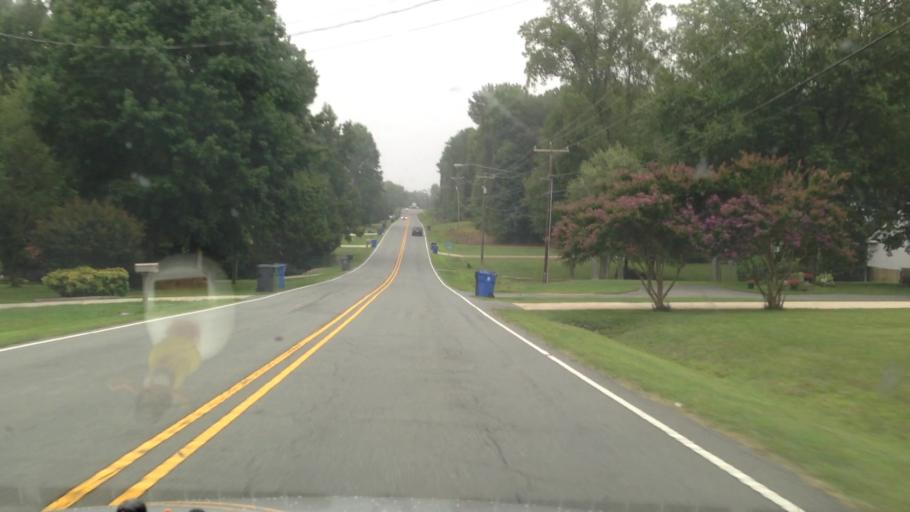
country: US
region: North Carolina
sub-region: Forsyth County
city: Kernersville
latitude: 36.1397
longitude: -80.0759
